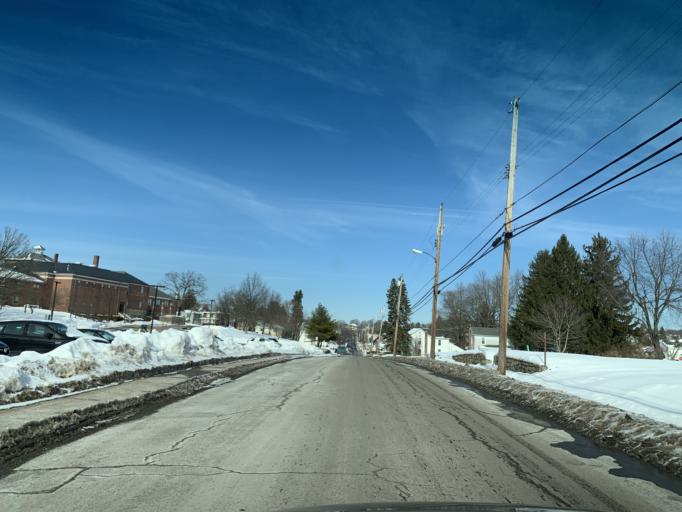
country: US
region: Maryland
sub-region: Allegany County
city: Frostburg
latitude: 39.6503
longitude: -78.9297
